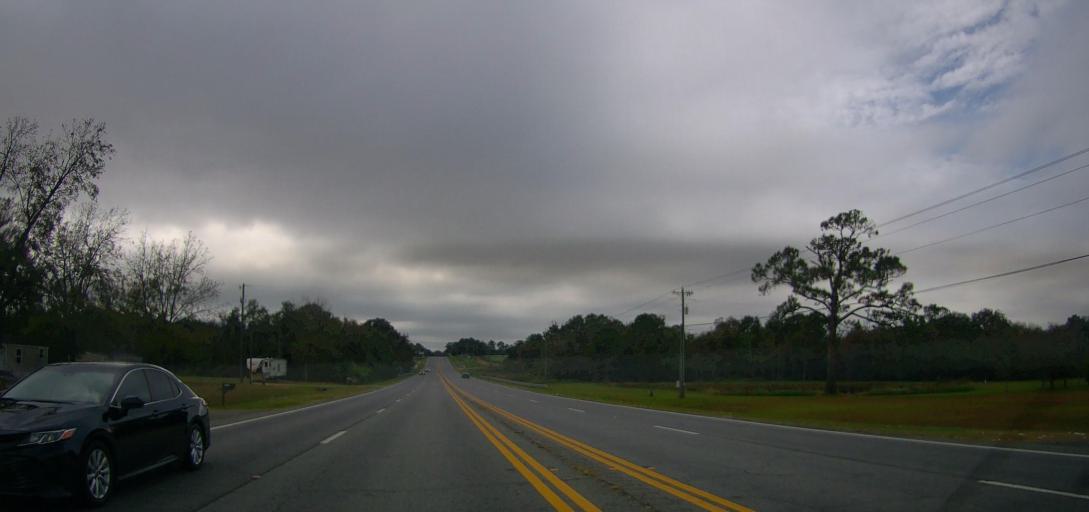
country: US
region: Georgia
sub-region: Tift County
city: Omega
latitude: 31.3520
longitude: -83.5847
